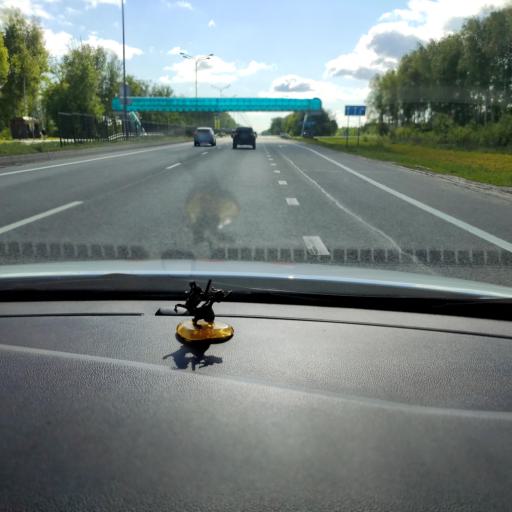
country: RU
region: Tatarstan
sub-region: Zelenodol'skiy Rayon
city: Vasil'yevo
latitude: 55.8699
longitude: 48.7153
